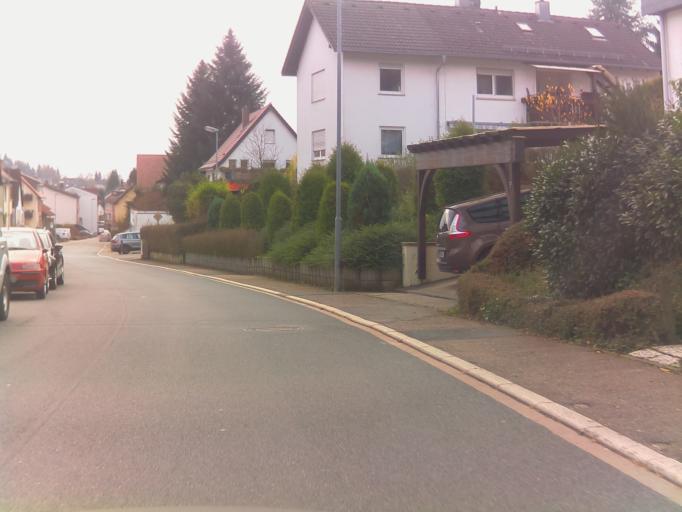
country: DE
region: Baden-Wuerttemberg
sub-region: Karlsruhe Region
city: Gaiberg
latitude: 49.3755
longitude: 8.7683
